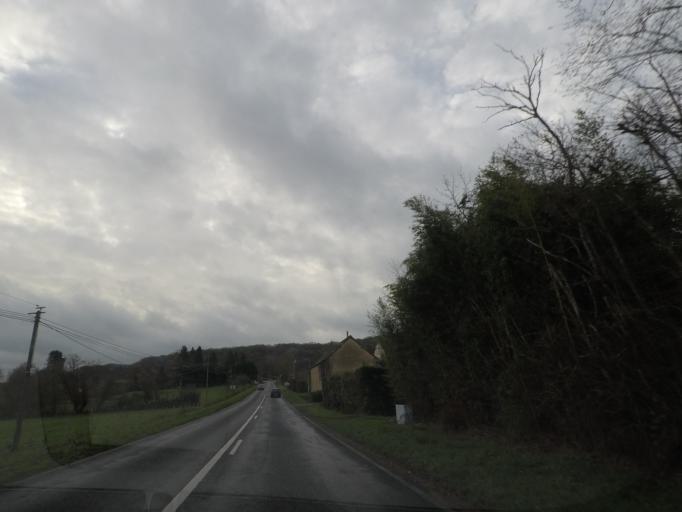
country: FR
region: Pays de la Loire
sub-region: Departement de la Sarthe
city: Vibraye
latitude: 48.0508
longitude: 0.7384
